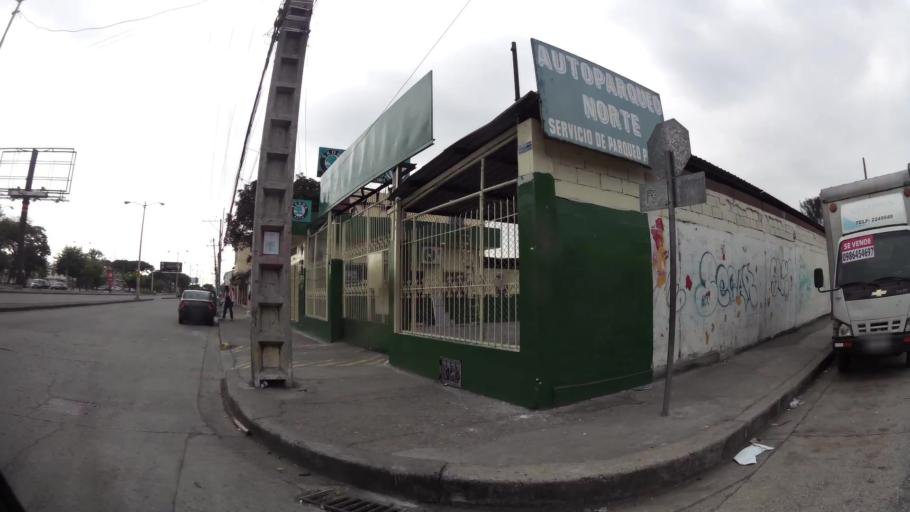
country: EC
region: Guayas
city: Eloy Alfaro
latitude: -2.1352
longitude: -79.8864
